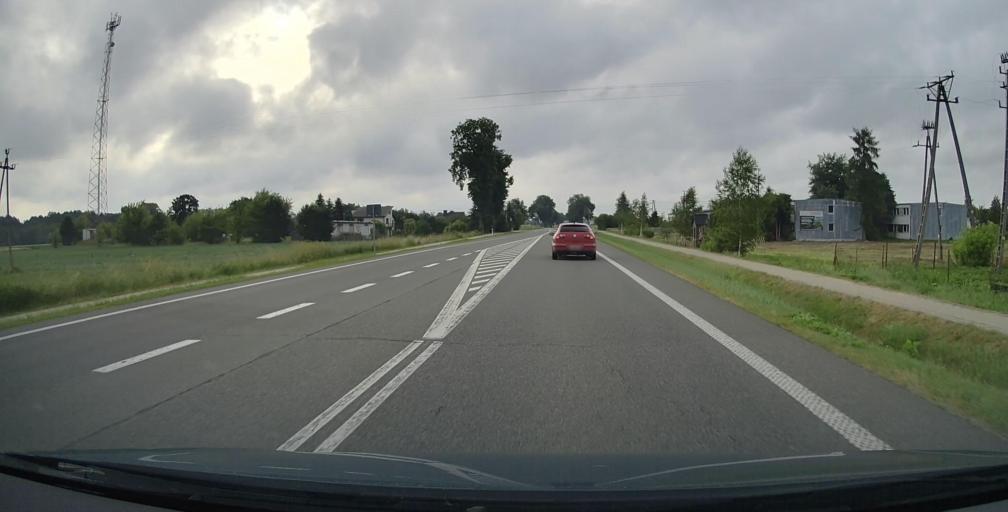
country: PL
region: Lublin Voivodeship
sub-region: Powiat lukowski
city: Trzebieszow
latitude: 52.0625
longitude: 22.5540
